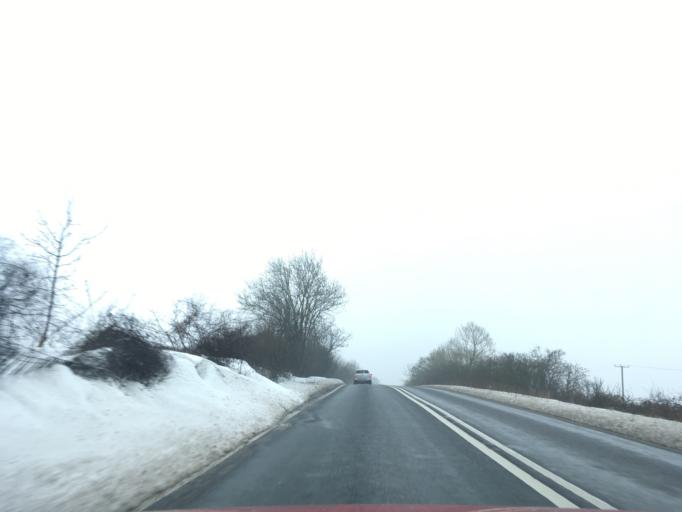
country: GB
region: England
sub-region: Warwickshire
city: Stratford-upon-Avon
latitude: 52.1999
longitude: -1.7671
